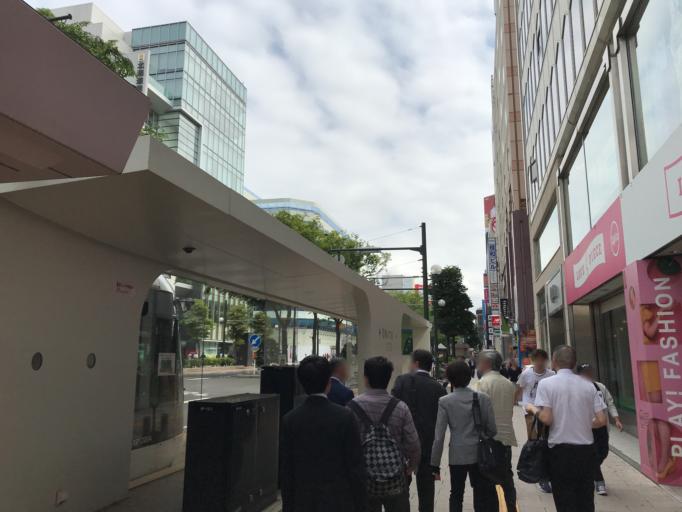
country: JP
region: Hokkaido
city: Sapporo
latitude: 43.0587
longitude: 141.3524
